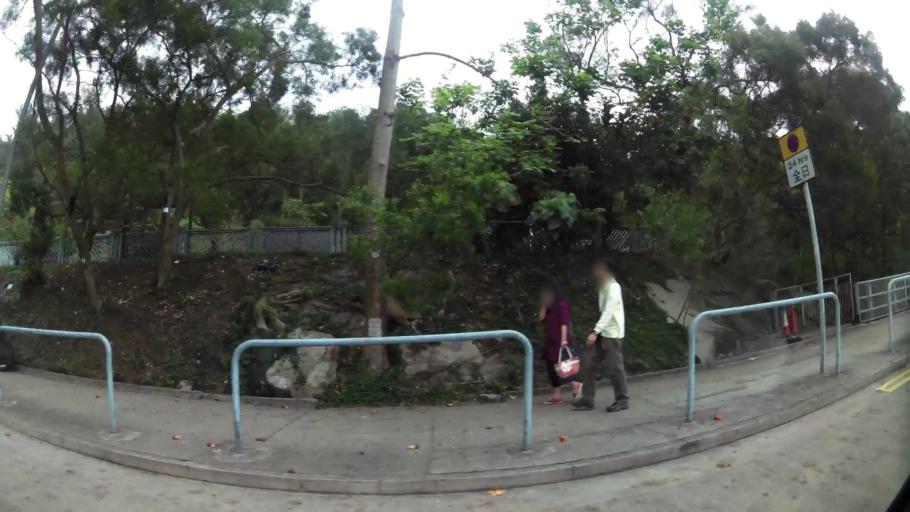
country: HK
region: Kowloon City
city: Kowloon
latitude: 22.3015
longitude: 114.2416
